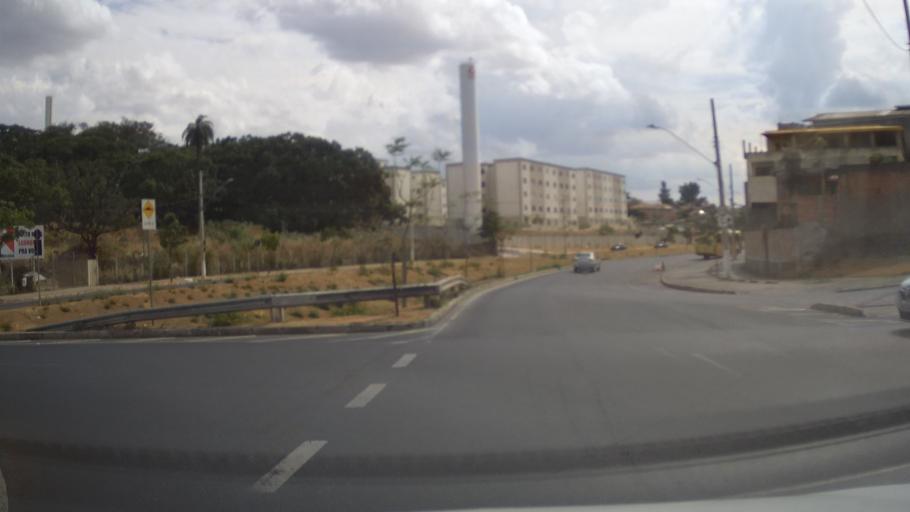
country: BR
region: Minas Gerais
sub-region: Belo Horizonte
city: Belo Horizonte
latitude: -19.8319
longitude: -43.9761
